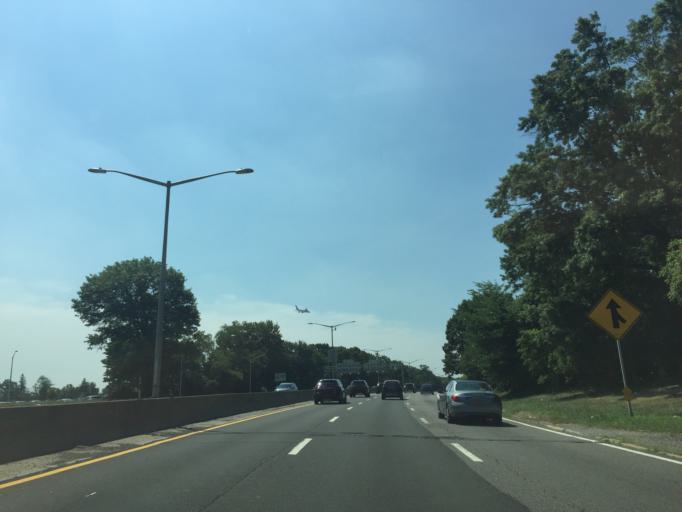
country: US
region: New York
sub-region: Nassau County
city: Bellerose Terrace
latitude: 40.7103
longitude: -73.7279
